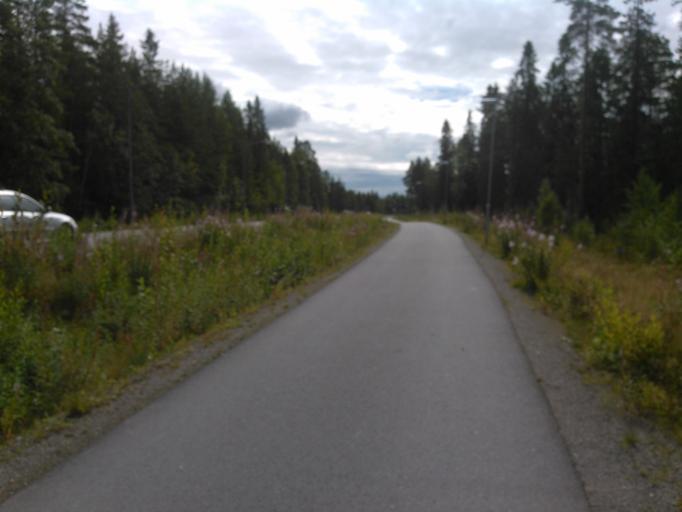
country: SE
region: Vaesterbotten
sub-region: Umea Kommun
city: Umea
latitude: 63.8235
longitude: 20.3138
